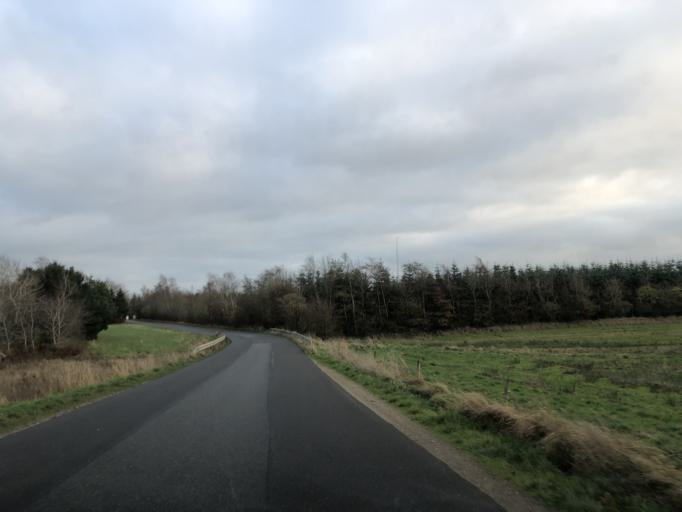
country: DK
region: Central Jutland
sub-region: Viborg Kommune
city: Viborg
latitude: 56.4761
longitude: 9.3410
